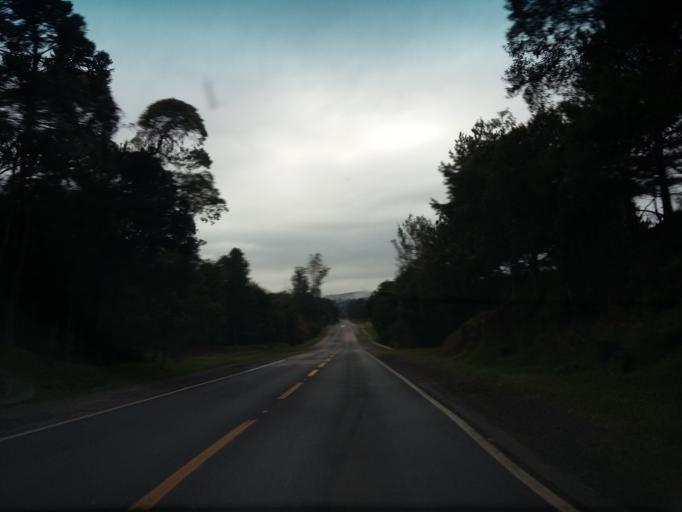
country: BR
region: Santa Catarina
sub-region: Santa Cecilia
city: Santa Cecilia
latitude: -26.7162
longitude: -50.3026
